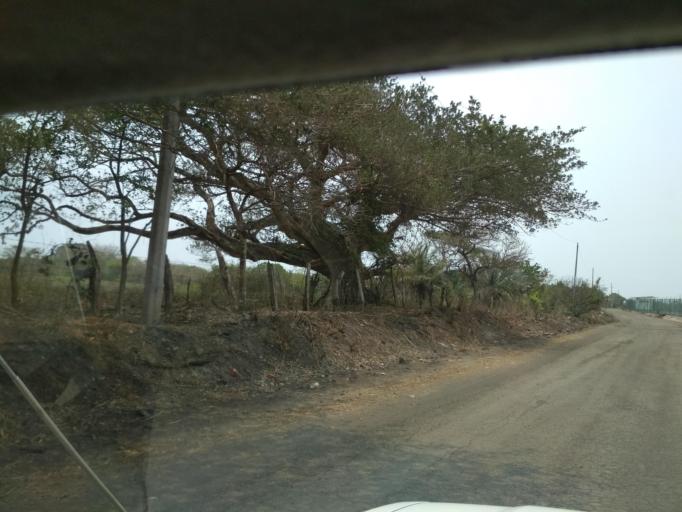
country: MX
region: Veracruz
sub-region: Veracruz
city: Delfino Victoria (Santa Fe)
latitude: 19.2005
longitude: -96.2647
